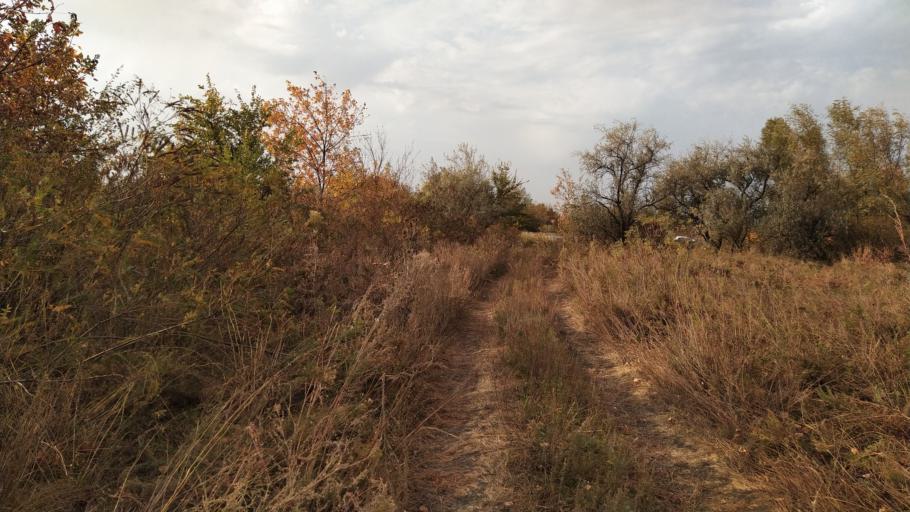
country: RU
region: Rostov
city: Kuleshovka
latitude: 47.1431
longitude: 39.5848
